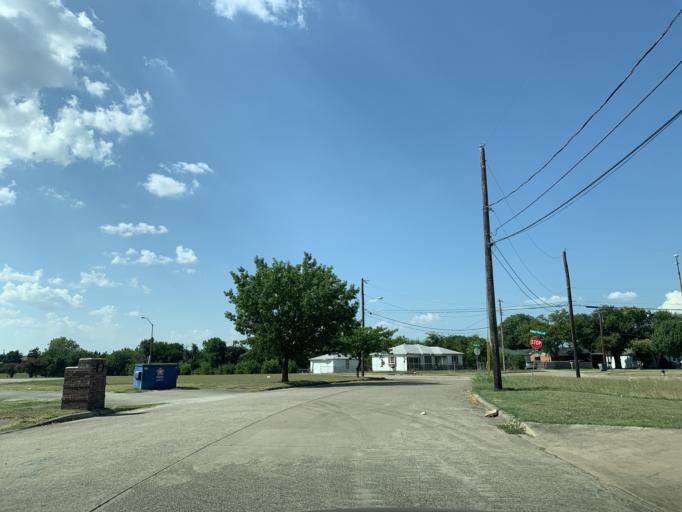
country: US
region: Texas
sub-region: Dallas County
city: Hutchins
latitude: 32.6552
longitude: -96.7745
